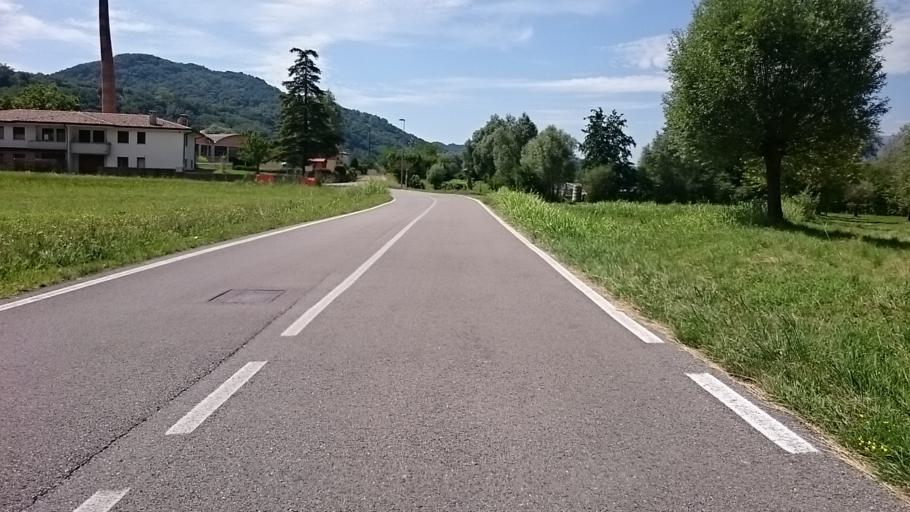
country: IT
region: Veneto
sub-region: Provincia di Treviso
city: Revine
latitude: 45.9961
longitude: 12.2515
